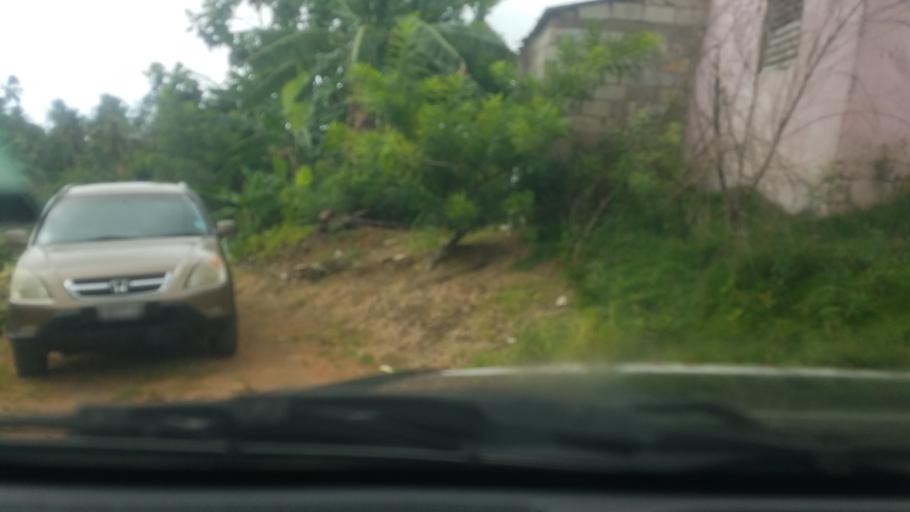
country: LC
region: Micoud Quarter
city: Micoud
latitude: 13.8044
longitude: -60.9458
